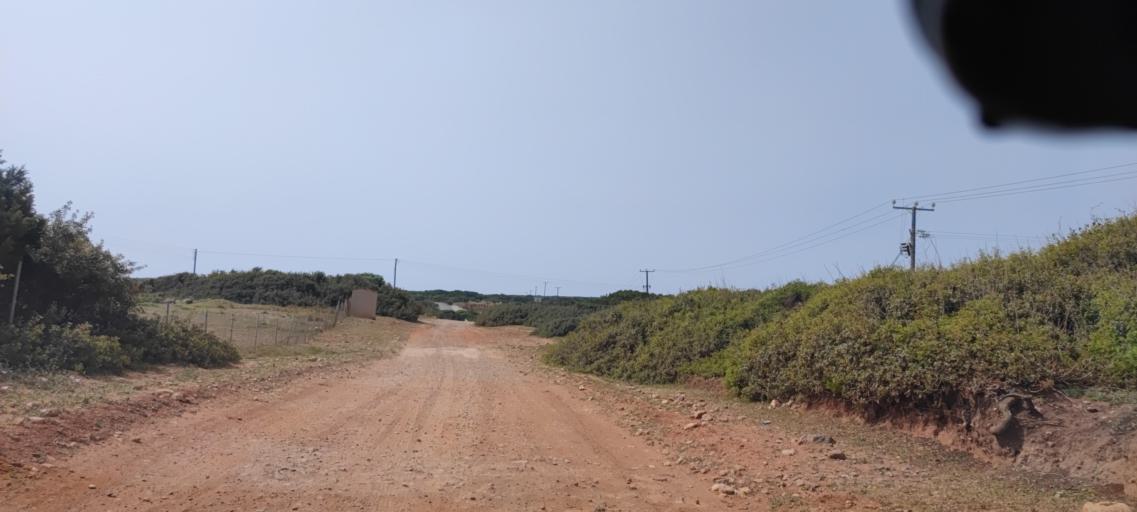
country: CY
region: Ammochostos
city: Rizokarpaso
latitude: 35.6689
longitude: 34.5721
